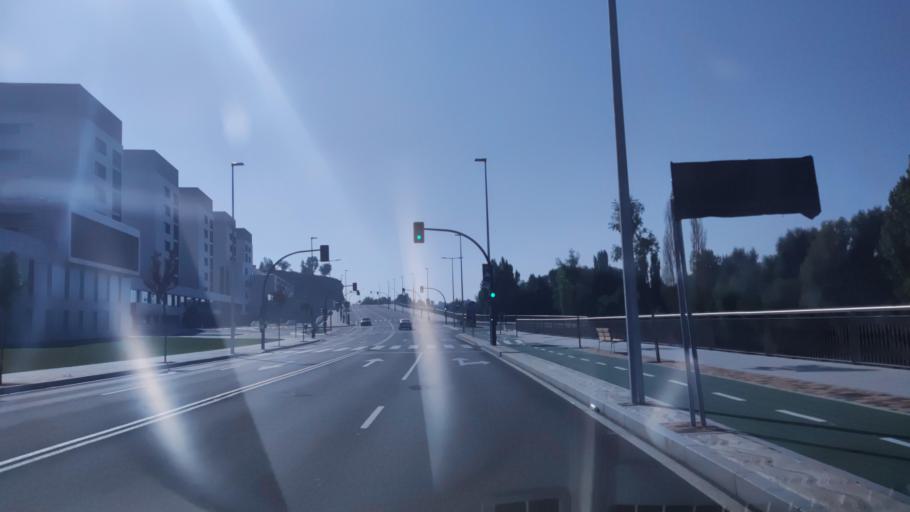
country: ES
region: Castille and Leon
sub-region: Provincia de Salamanca
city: Salamanca
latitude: 40.9636
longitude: -5.6783
